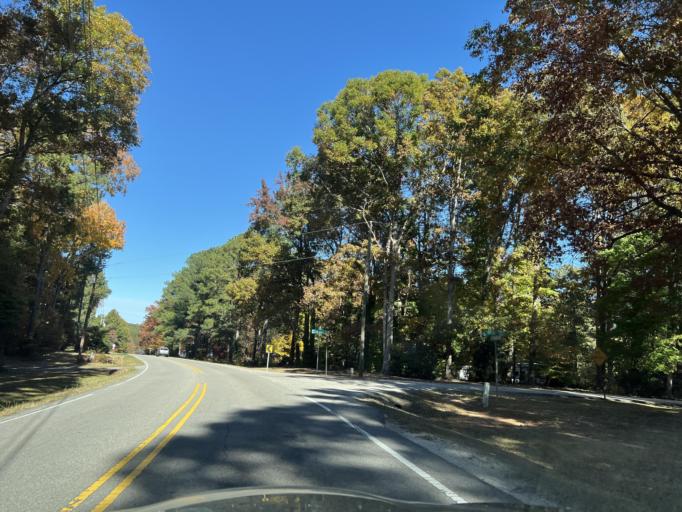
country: US
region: North Carolina
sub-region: Wake County
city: Garner
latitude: 35.6873
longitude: -78.6941
